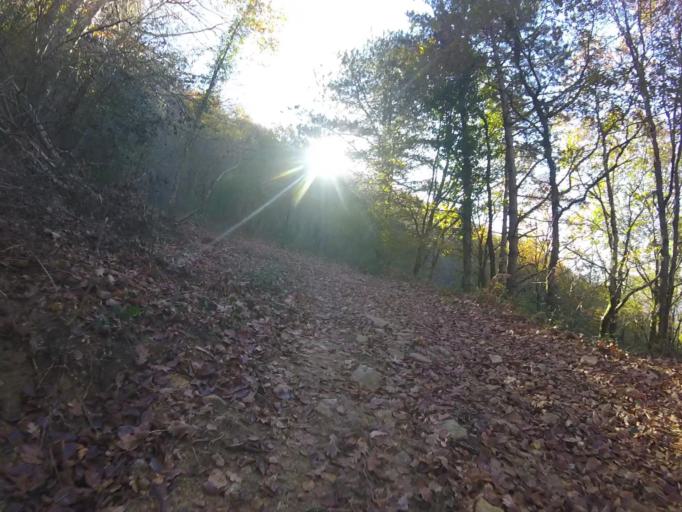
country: ES
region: Navarre
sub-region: Provincia de Navarra
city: Bera
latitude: 43.3142
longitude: -1.7197
